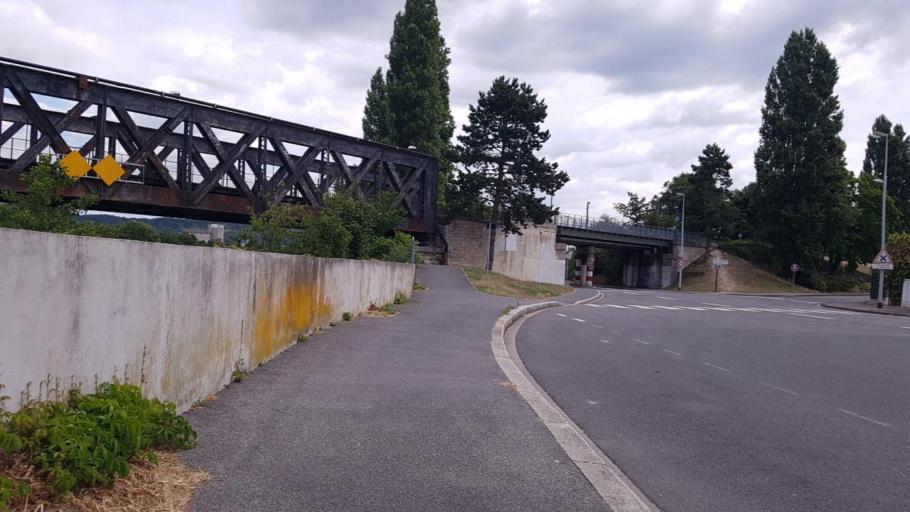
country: FR
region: Picardie
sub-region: Departement de l'Oise
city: Compiegne
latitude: 49.4268
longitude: 2.8351
